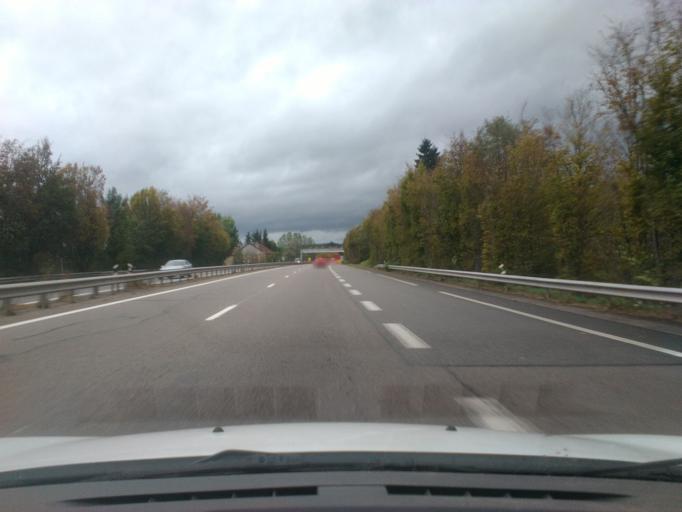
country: FR
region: Lorraine
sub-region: Departement des Vosges
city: Saint-Michel-sur-Meurthe
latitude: 48.3128
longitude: 6.9192
